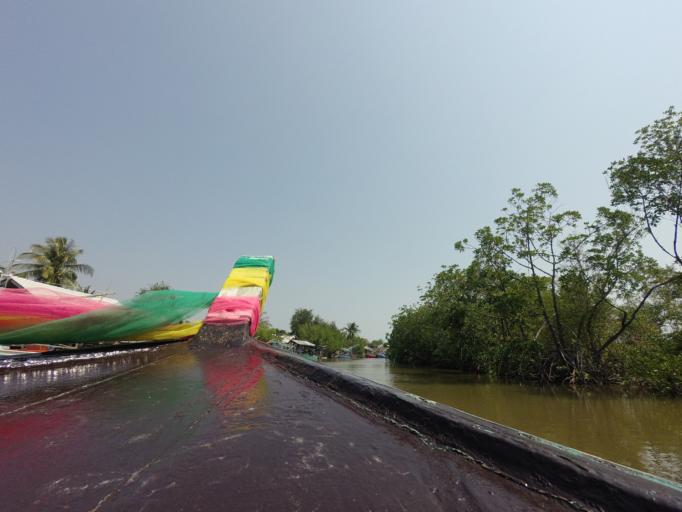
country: TH
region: Prachuap Khiri Khan
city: Kui Buri
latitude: 12.1360
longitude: 99.9654
